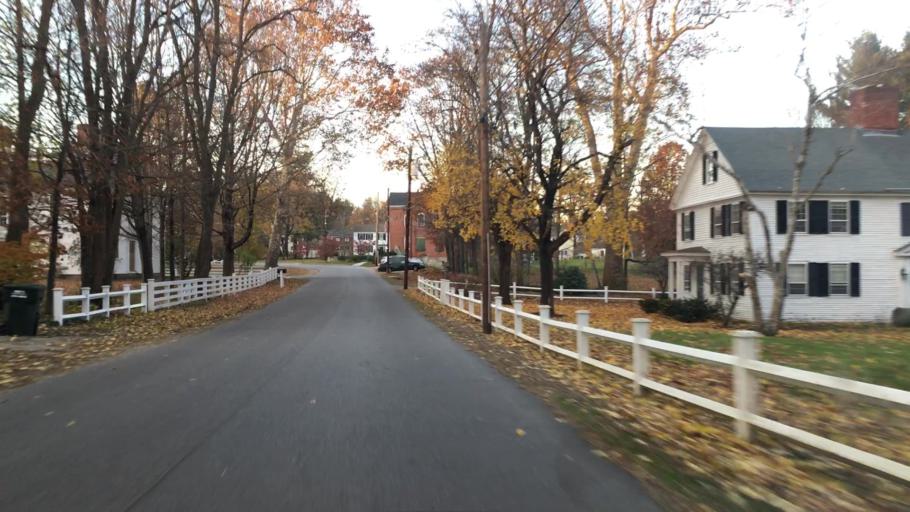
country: US
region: New Hampshire
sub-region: Hillsborough County
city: Milford
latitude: 42.8632
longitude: -71.6236
